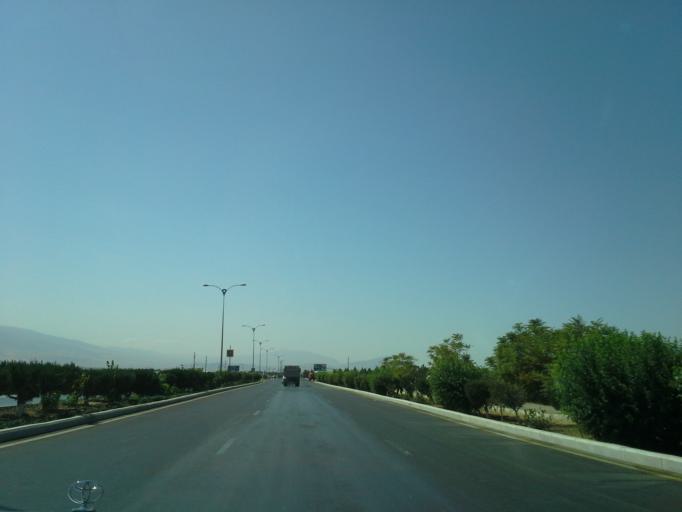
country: TM
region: Ahal
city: Annau
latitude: 37.9065
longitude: 58.5253
